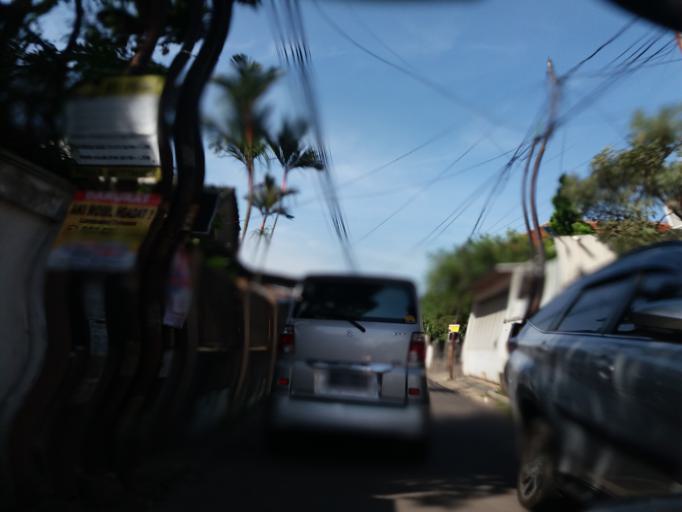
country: ID
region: West Java
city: Bandung
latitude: -6.9433
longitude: 107.6115
